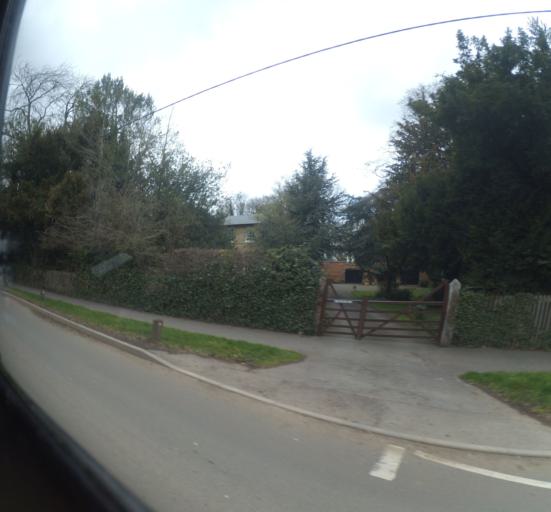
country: GB
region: England
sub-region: Warwickshire
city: Brandon
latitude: 52.4100
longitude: -1.3645
